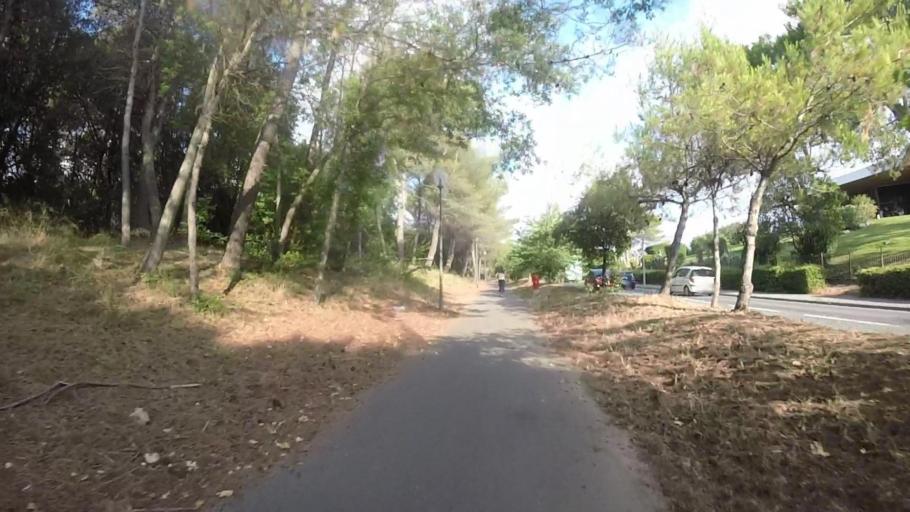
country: FR
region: Provence-Alpes-Cote d'Azur
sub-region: Departement des Alpes-Maritimes
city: Biot
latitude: 43.6166
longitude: 7.0630
